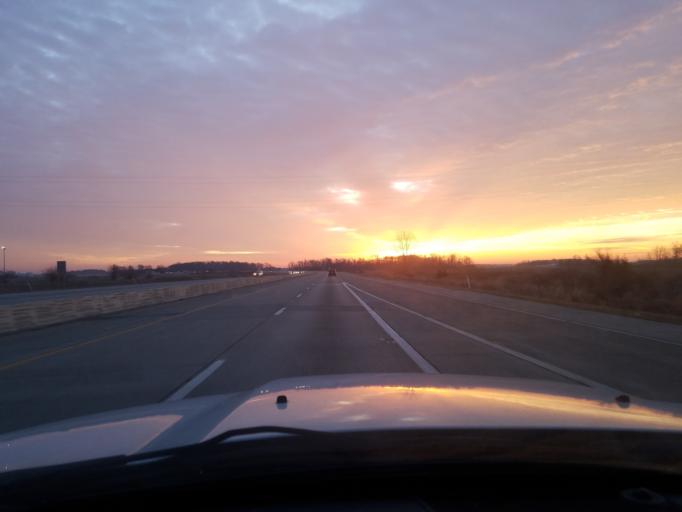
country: US
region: Indiana
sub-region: Wells County
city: Ossian
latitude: 40.9535
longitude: -85.2558
